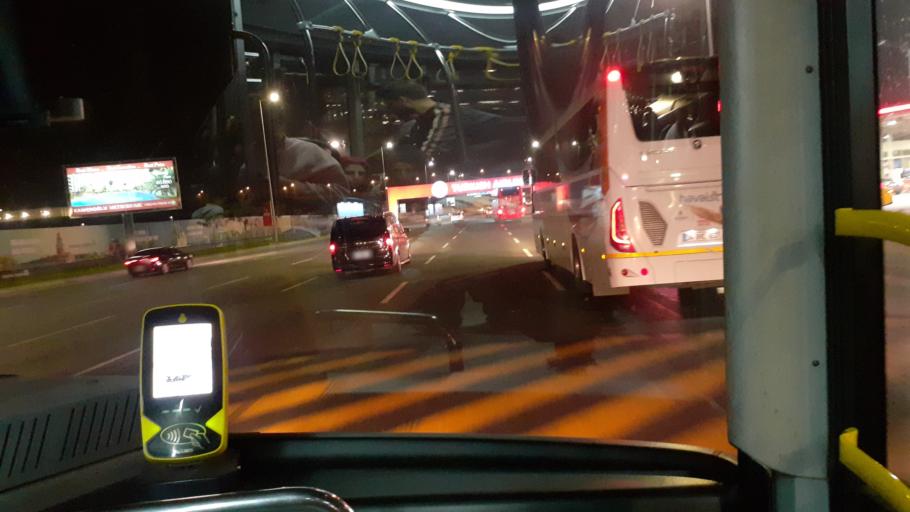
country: TR
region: Istanbul
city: Durusu
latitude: 41.2525
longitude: 28.7388
